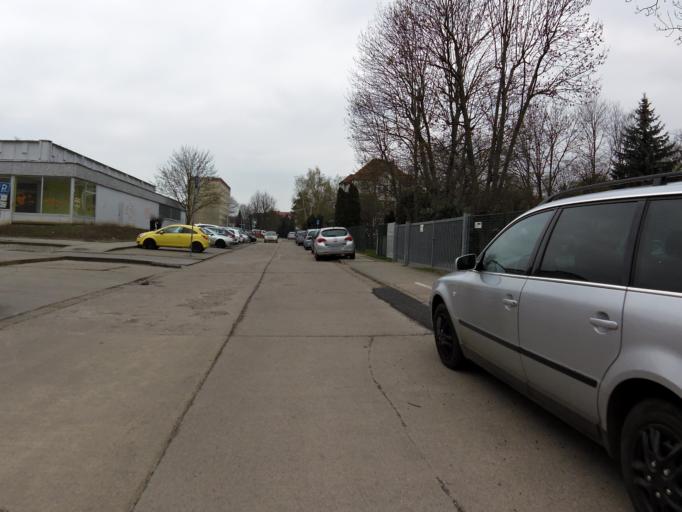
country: DE
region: Thuringia
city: Gotha
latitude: 50.9521
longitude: 10.7028
